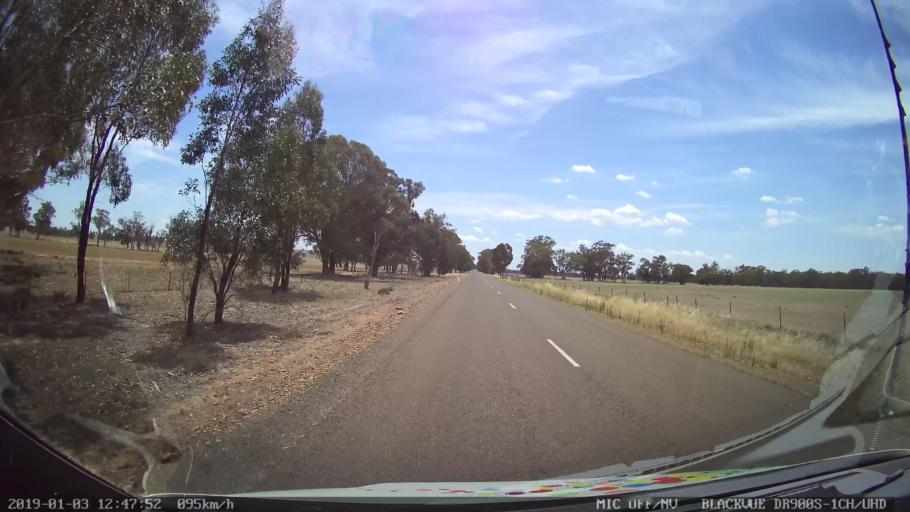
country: AU
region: New South Wales
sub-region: Weddin
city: Grenfell
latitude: -33.7215
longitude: 148.2456
